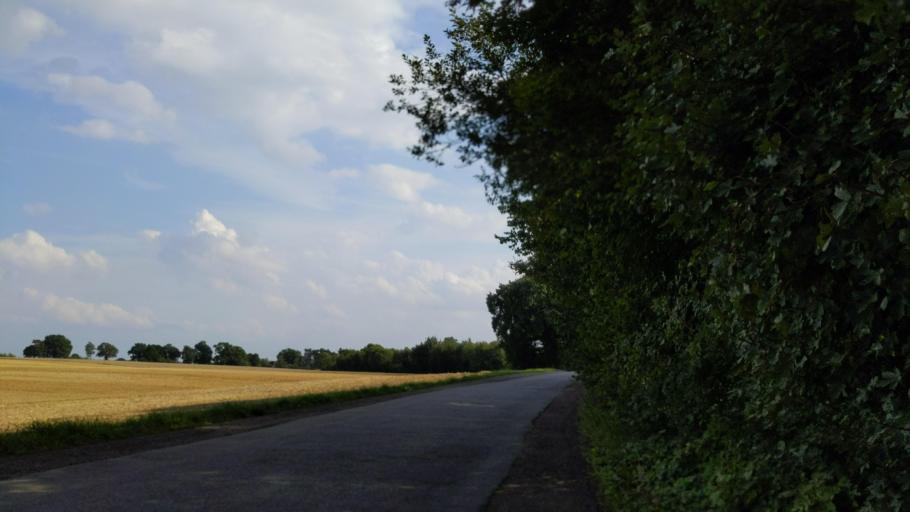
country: DE
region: Schleswig-Holstein
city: Eutin
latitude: 54.1201
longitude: 10.5902
